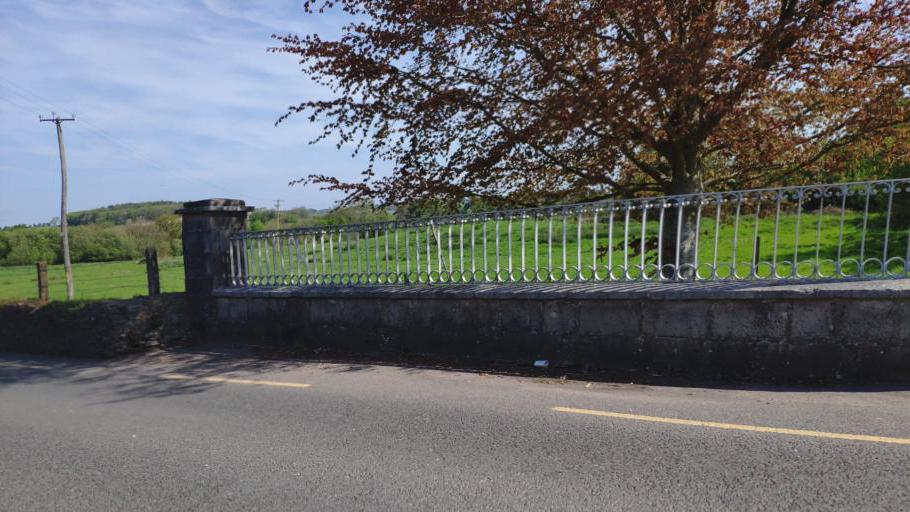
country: IE
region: Munster
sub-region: County Cork
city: Blarney
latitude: 51.9261
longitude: -8.5563
